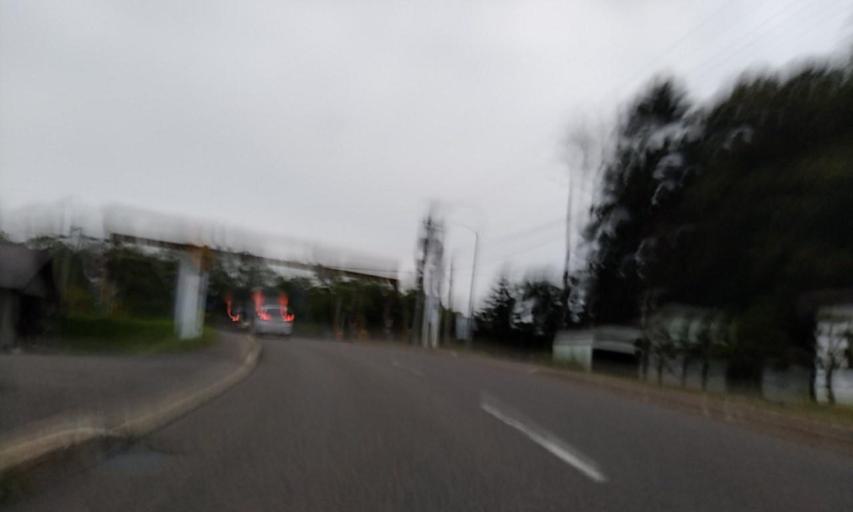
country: JP
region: Hokkaido
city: Abashiri
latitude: 44.0037
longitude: 144.2311
